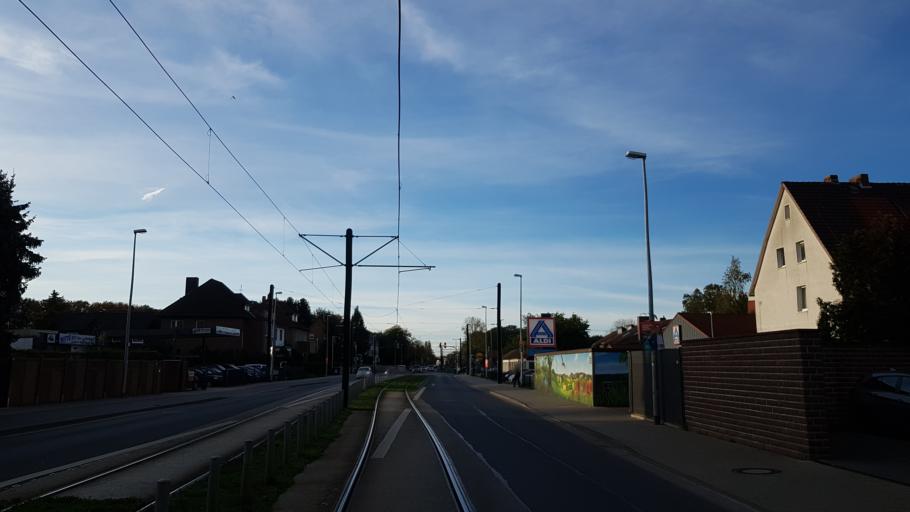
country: DE
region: Lower Saxony
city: Isernhagen Farster Bauerschaft
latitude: 52.3932
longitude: 9.8467
